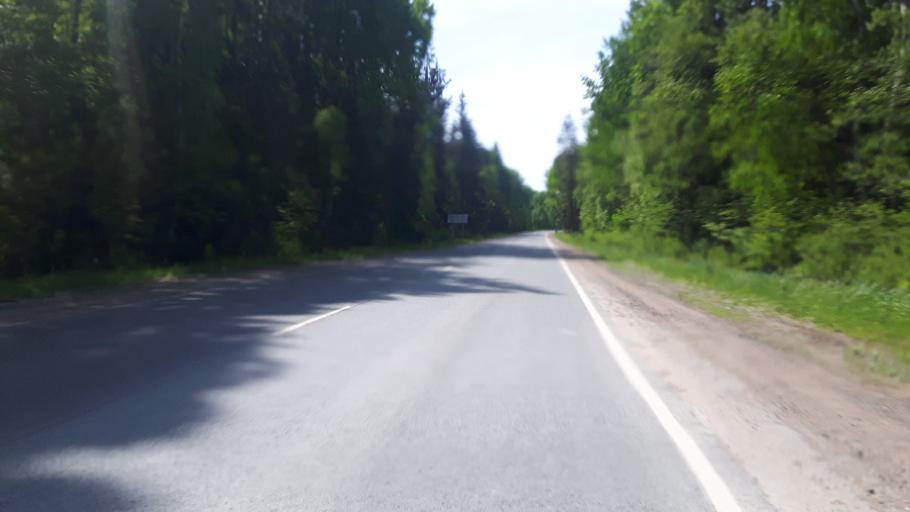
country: RU
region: Leningrad
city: Vistino
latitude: 59.6900
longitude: 28.4614
